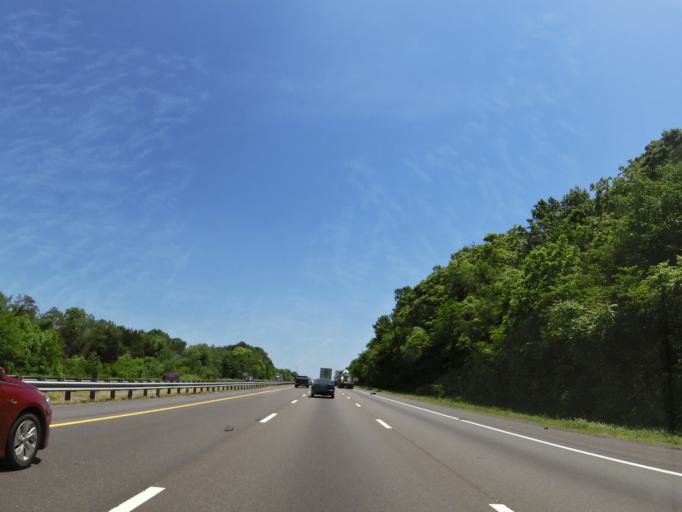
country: US
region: Tennessee
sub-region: Jefferson County
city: Dandridge
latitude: 36.0155
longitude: -83.5066
